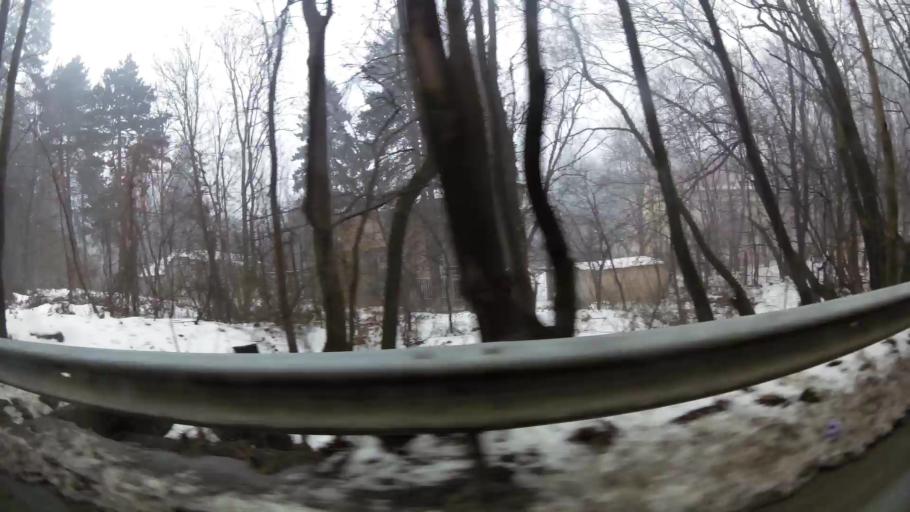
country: BG
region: Sofia-Capital
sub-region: Stolichna Obshtina
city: Sofia
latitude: 42.6572
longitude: 23.2417
